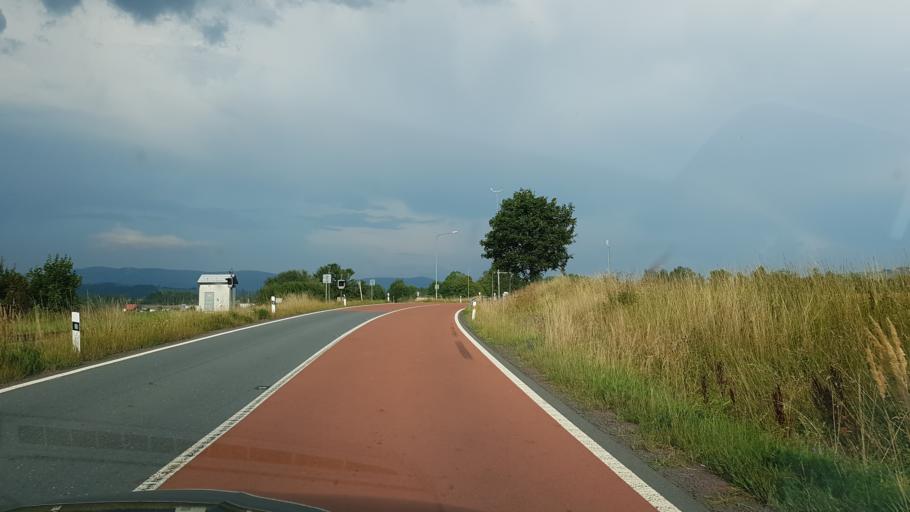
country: CZ
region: Pardubicky
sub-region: Okres Usti nad Orlici
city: Kraliky
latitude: 50.0896
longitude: 16.7130
